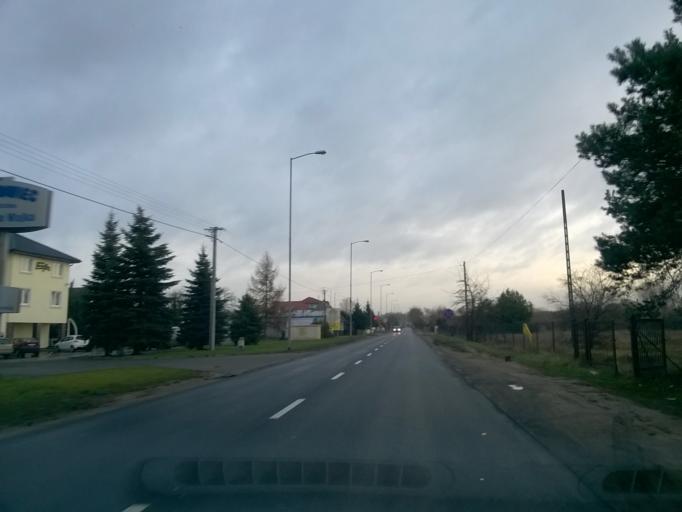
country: PL
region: Greater Poland Voivodeship
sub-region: Powiat wagrowiecki
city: Wagrowiec
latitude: 52.8250
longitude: 17.2337
